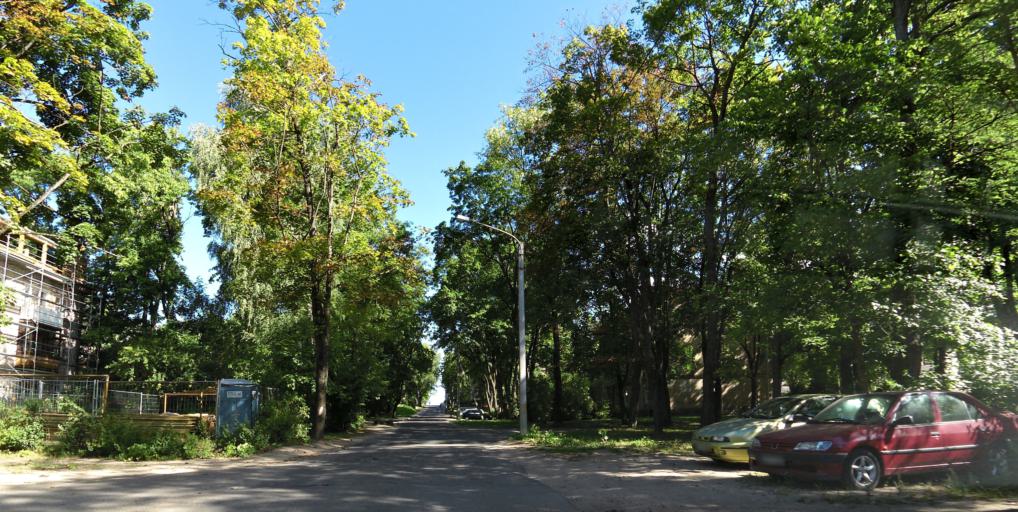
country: LT
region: Vilnius County
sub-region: Vilnius
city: Vilnius
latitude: 54.7057
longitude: 25.2923
